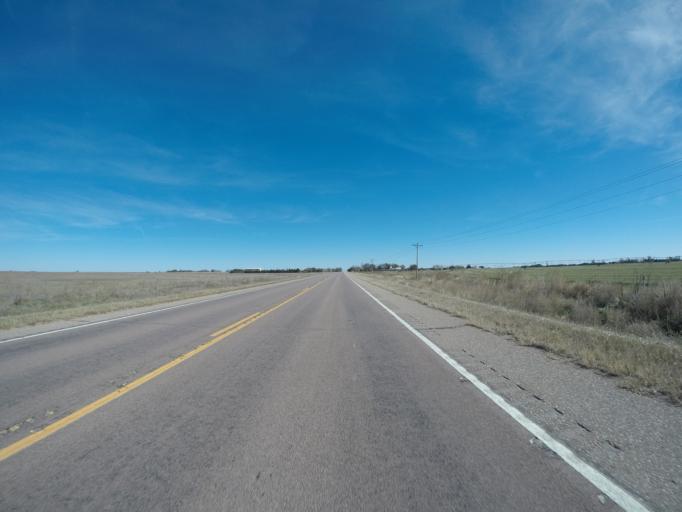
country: US
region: Colorado
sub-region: Yuma County
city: Yuma
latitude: 39.6560
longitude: -102.6934
